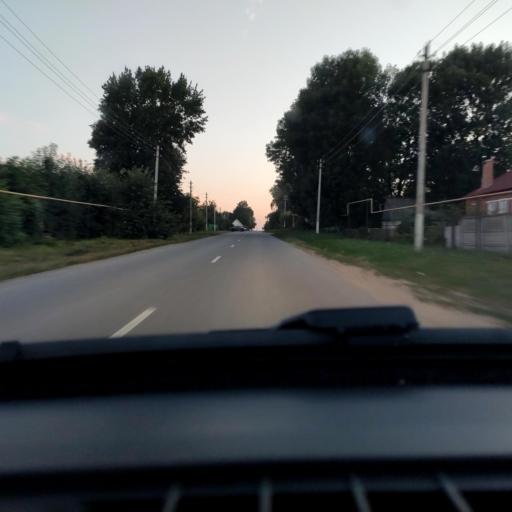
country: RU
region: Lipetsk
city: Zadonsk
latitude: 52.2865
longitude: 38.7482
